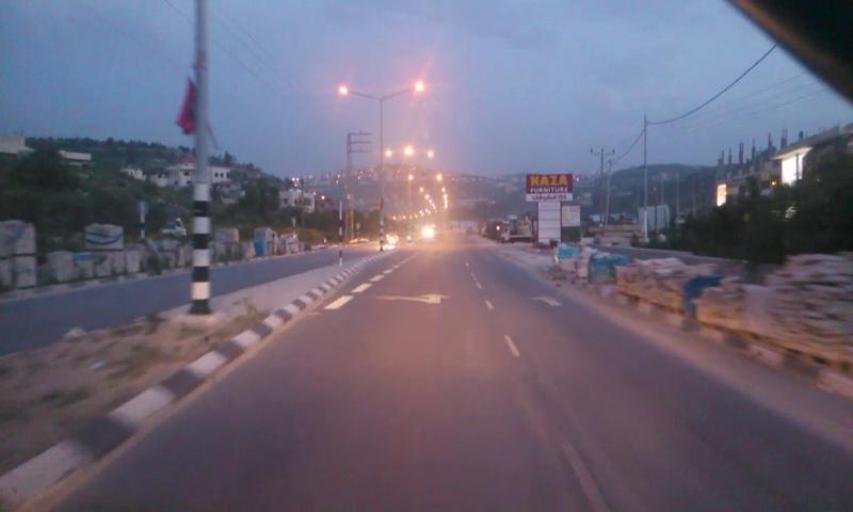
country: PS
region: West Bank
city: Dayr Sharaf
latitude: 32.2478
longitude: 35.1917
